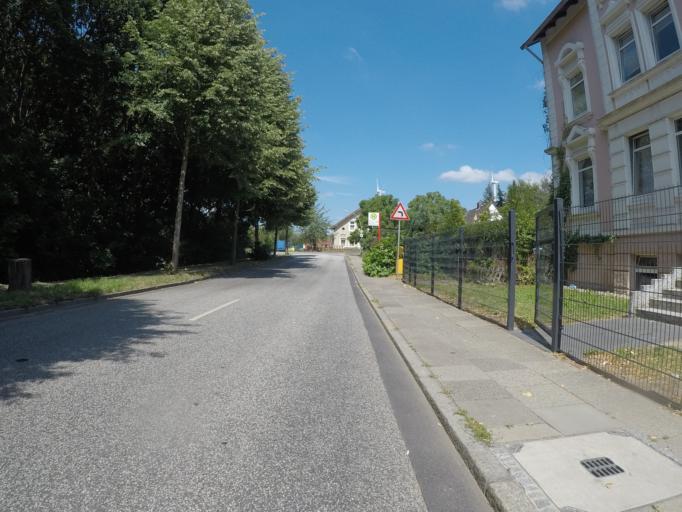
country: DE
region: Hamburg
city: Rothenburgsort
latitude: 53.5031
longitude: 10.0272
